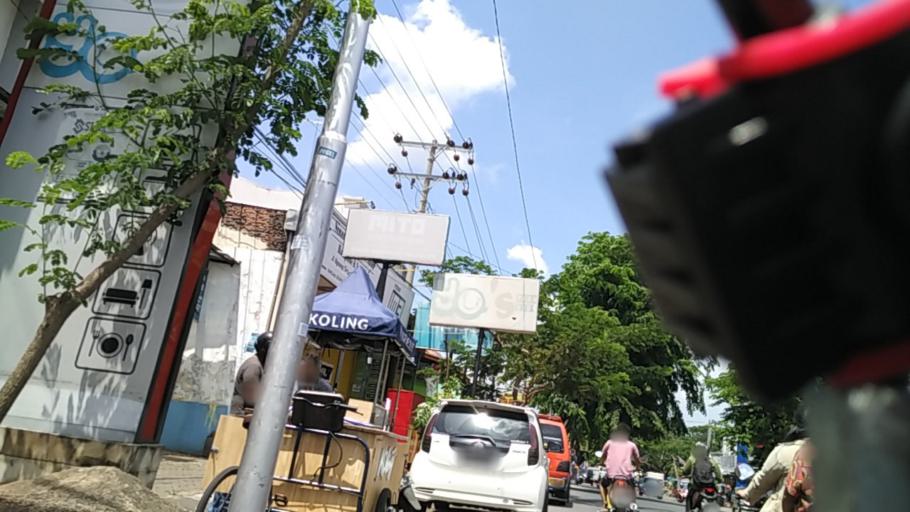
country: ID
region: Central Java
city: Semarang
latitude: -7.0520
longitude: 110.4271
